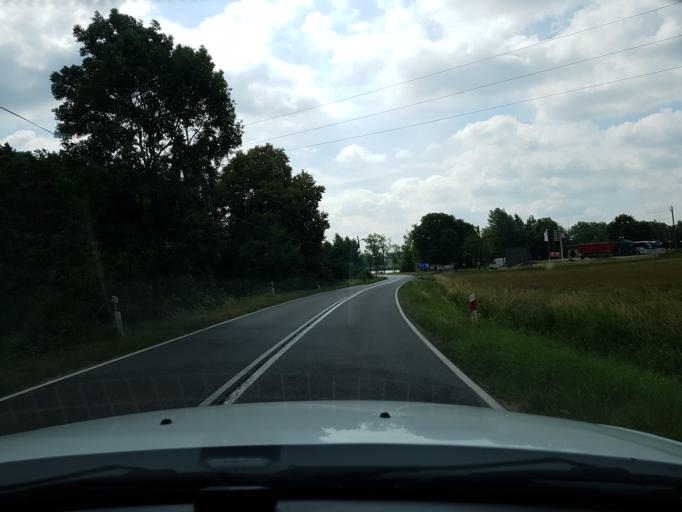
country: PL
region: West Pomeranian Voivodeship
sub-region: Powiat gryfinski
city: Banie
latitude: 53.1031
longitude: 14.6509
